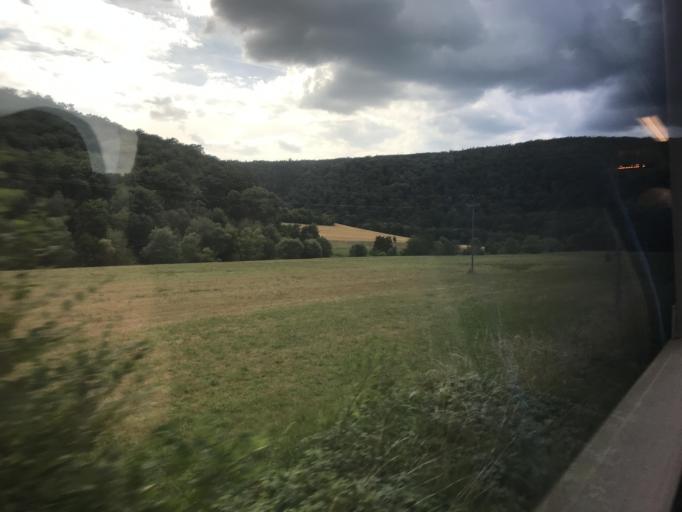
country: DE
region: Bavaria
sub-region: Regierungsbezirk Unterfranken
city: Schonau
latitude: 50.0868
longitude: 9.7237
